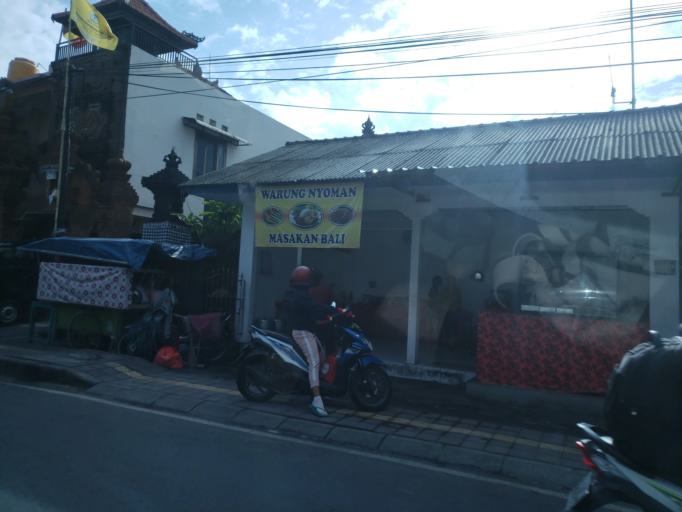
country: ID
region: Bali
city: Kuta
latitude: -8.6807
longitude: 115.1778
